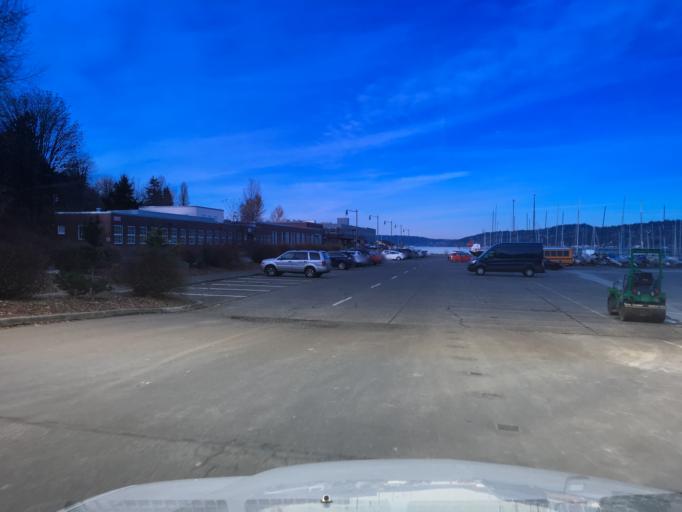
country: US
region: Washington
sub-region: King County
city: Inglewood-Finn Hill
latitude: 47.6867
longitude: -122.2645
